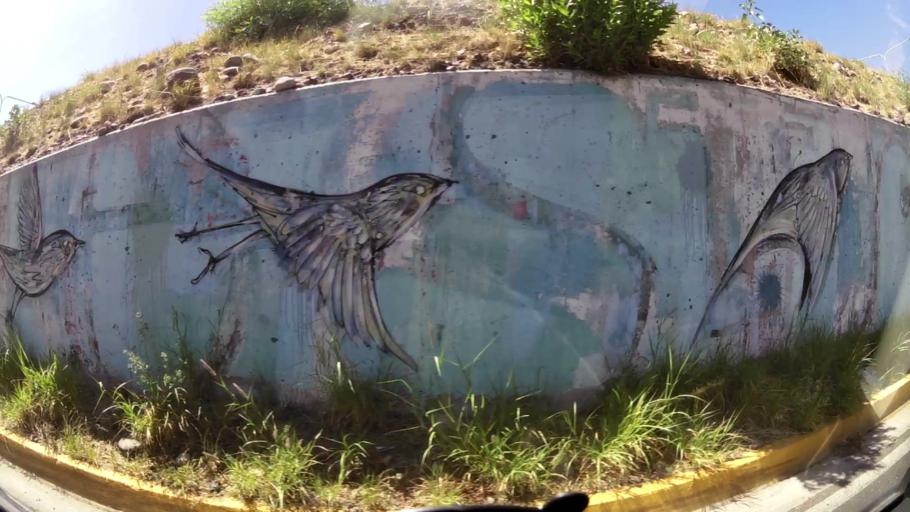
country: AR
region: Mendoza
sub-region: Departamento de Godoy Cruz
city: Godoy Cruz
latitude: -32.9318
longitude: -68.8639
